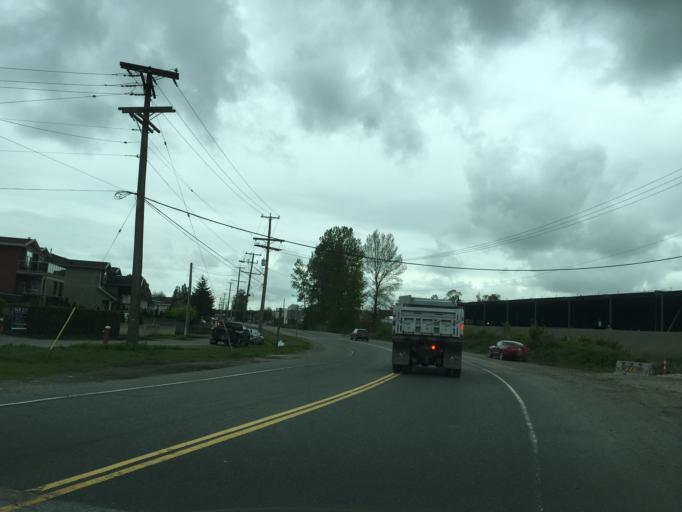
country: CA
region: British Columbia
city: New Westminster
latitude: 49.1947
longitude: -122.9372
